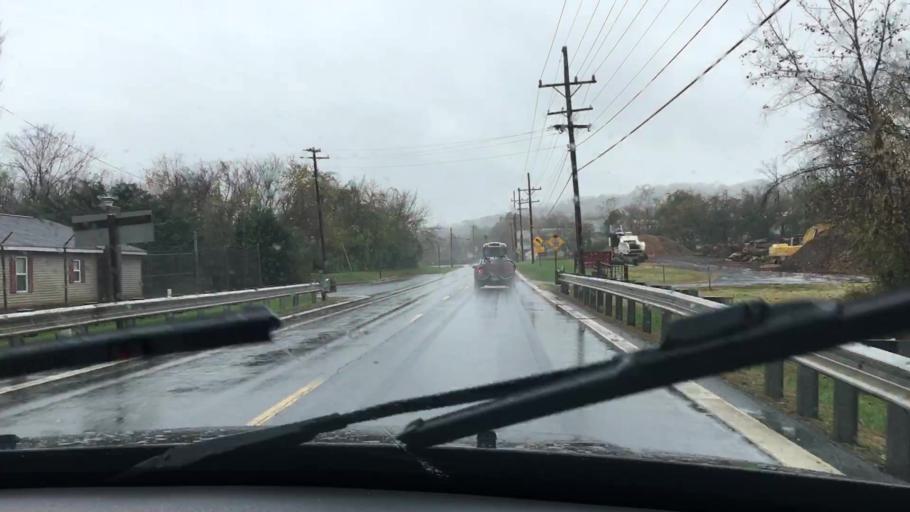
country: US
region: Maryland
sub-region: Frederick County
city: Point of Rocks
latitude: 39.2755
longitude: -77.5241
